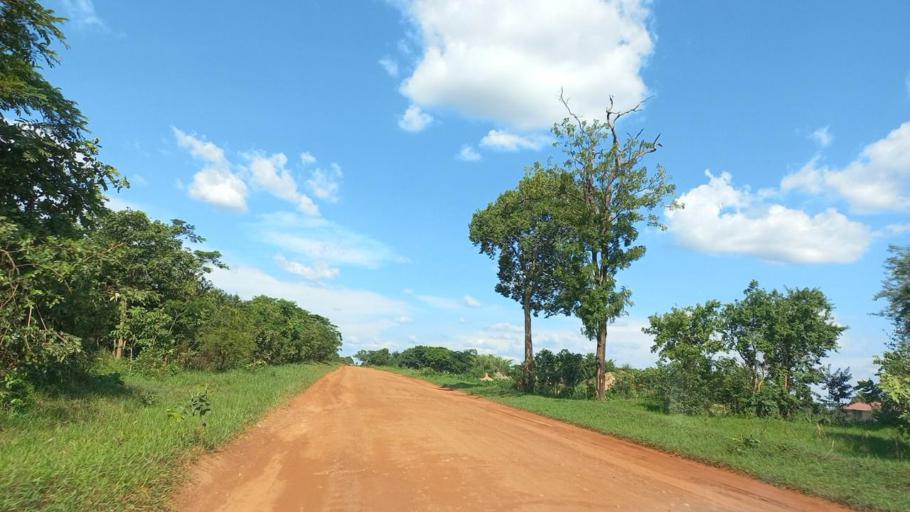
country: ZM
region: Copperbelt
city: Kitwe
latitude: -12.8684
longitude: 28.3645
